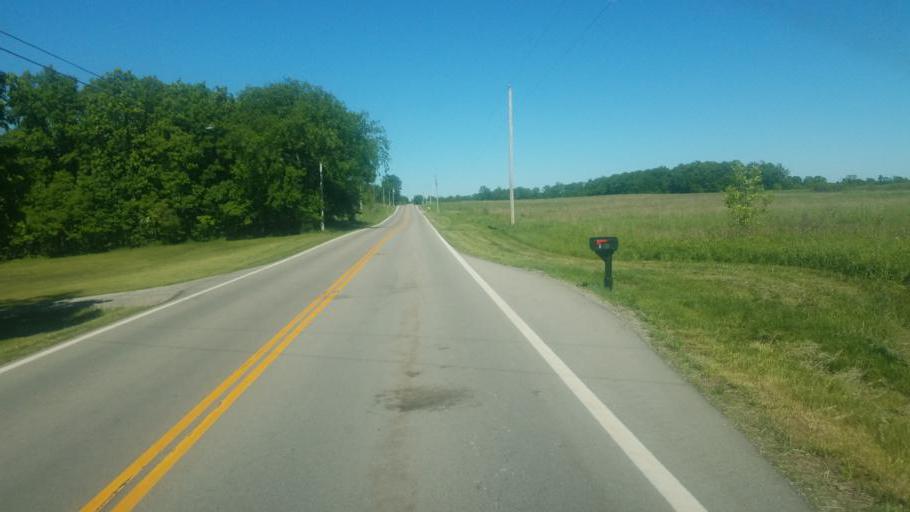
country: US
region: Ohio
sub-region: Logan County
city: Northwood
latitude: 40.4583
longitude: -83.6923
